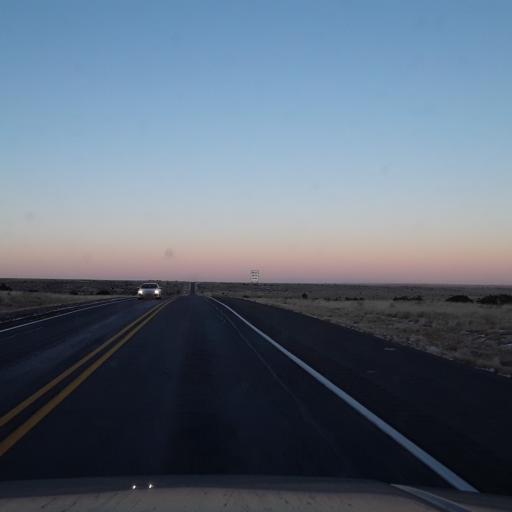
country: US
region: New Mexico
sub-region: Guadalupe County
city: Santa Rosa
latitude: 34.5332
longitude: -105.3177
